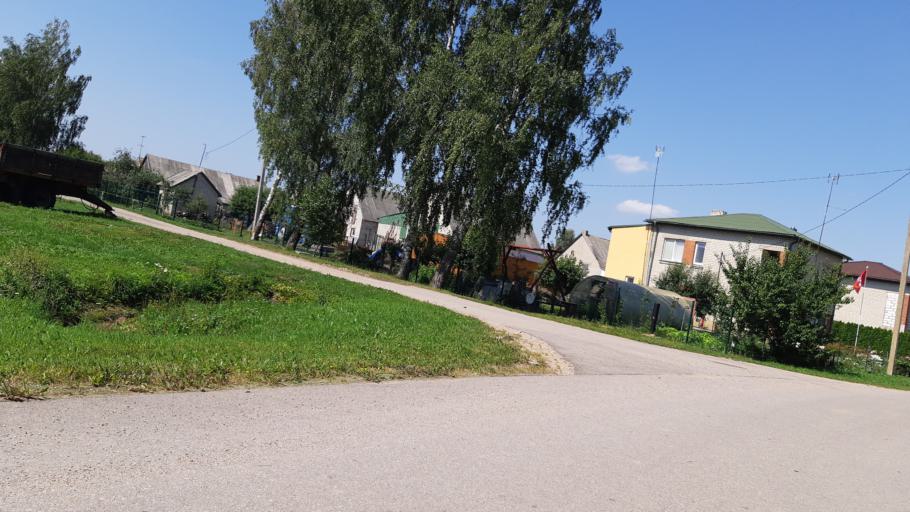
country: LT
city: Virbalis
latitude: 54.6208
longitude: 22.8164
